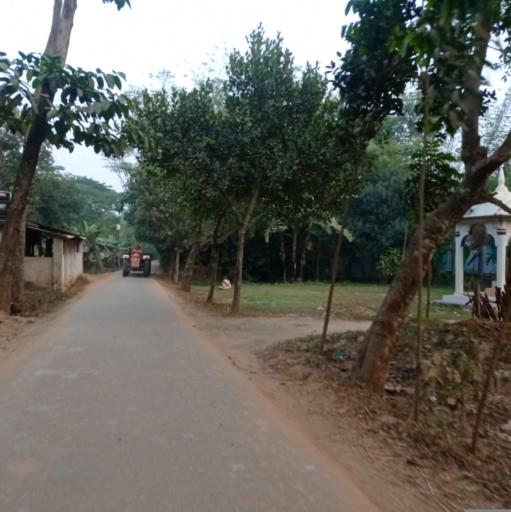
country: BD
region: Dhaka
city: Bajitpur
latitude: 24.1326
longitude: 90.8159
